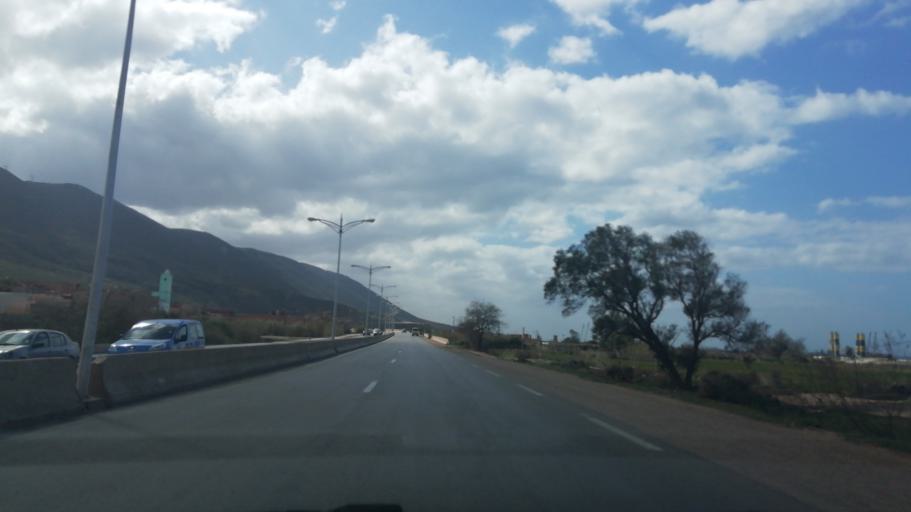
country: DZ
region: Mostaganem
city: Mostaganem
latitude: 36.0240
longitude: 0.1330
